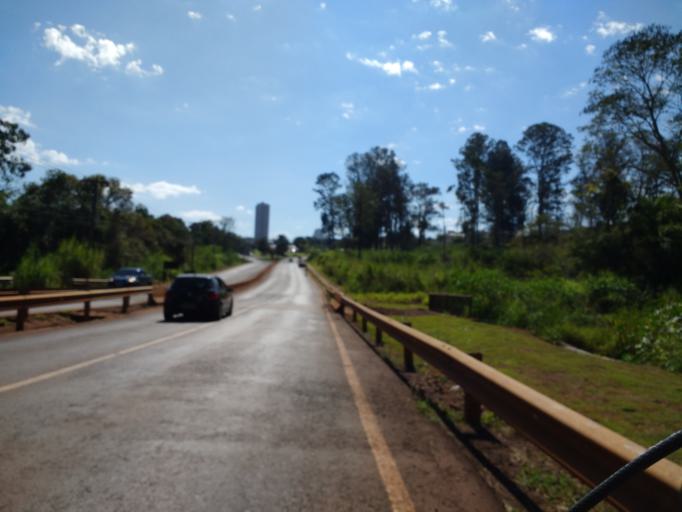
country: BR
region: Parana
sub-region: Londrina
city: Londrina
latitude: -23.3532
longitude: -51.1918
